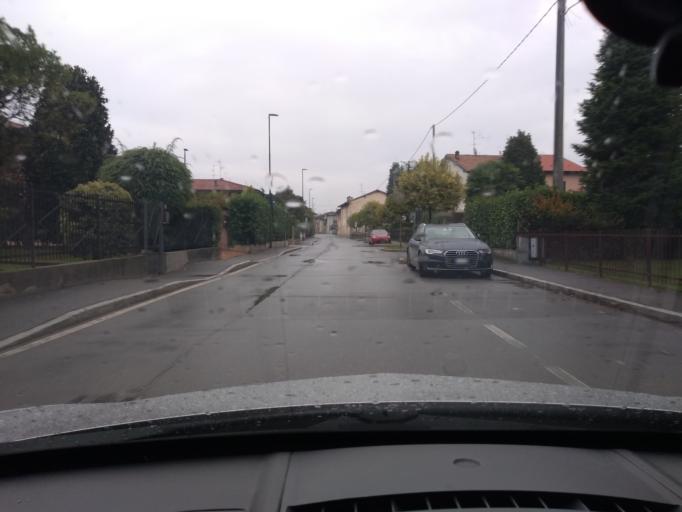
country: IT
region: Lombardy
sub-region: Provincia di Bergamo
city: Mornico al Serio
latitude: 45.5907
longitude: 9.8013
